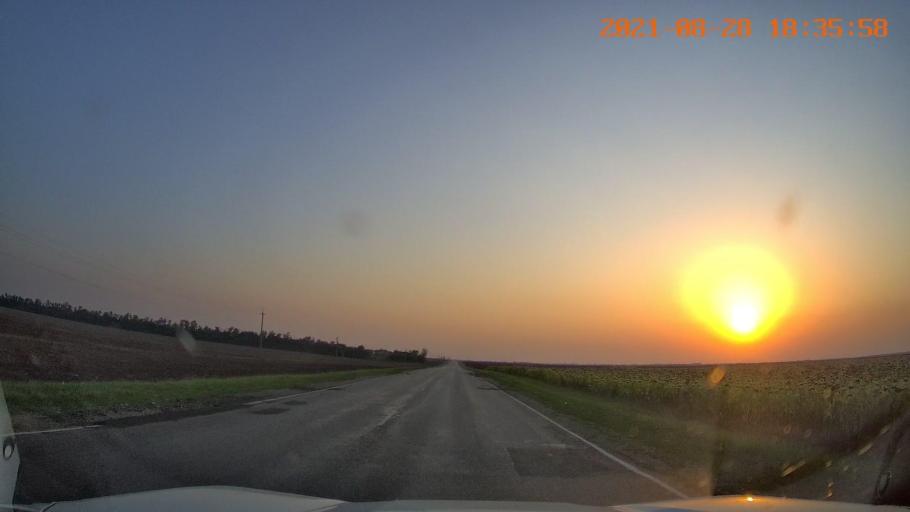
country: RU
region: Adygeya
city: Giaginskaya
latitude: 44.8697
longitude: 40.1224
